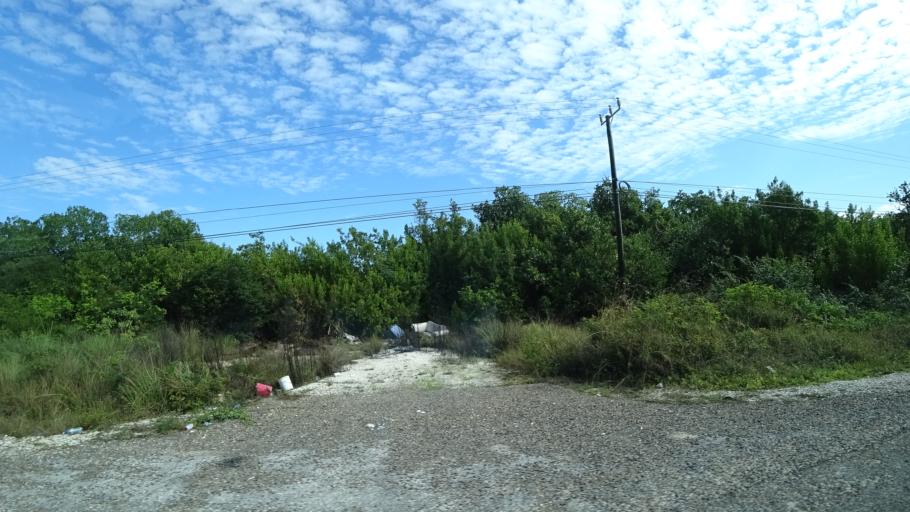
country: BZ
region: Belize
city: Belize City
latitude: 17.5425
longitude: -88.2544
